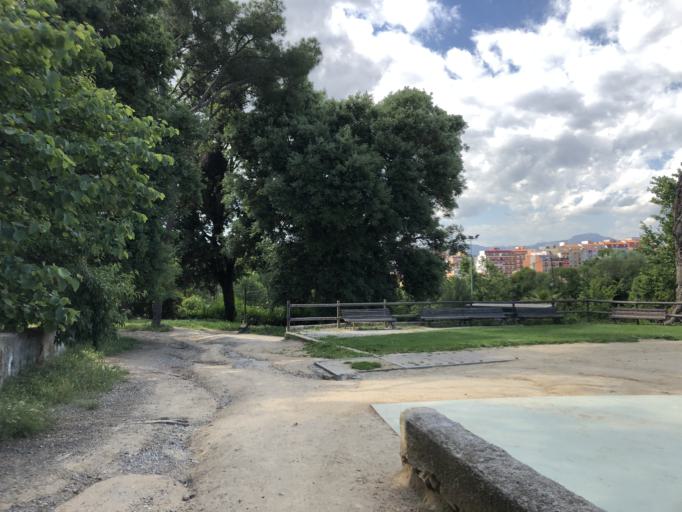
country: ES
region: Catalonia
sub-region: Provincia de Barcelona
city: Rubi
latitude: 41.4930
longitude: 2.0412
